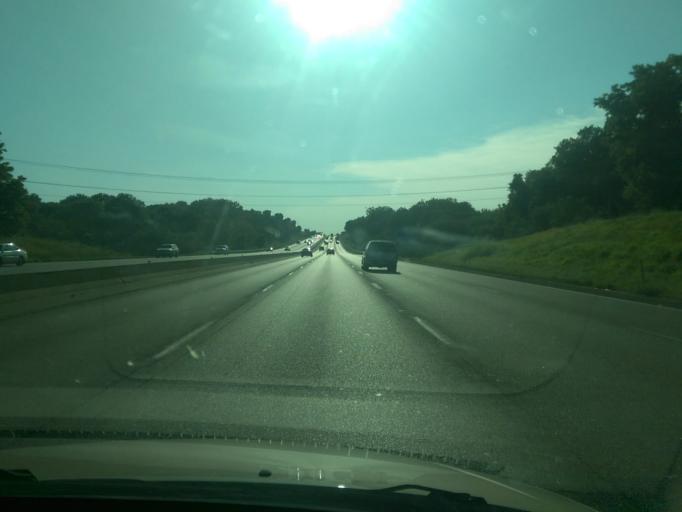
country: US
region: Missouri
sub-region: Jackson County
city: Independence
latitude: 39.0451
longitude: -94.3910
